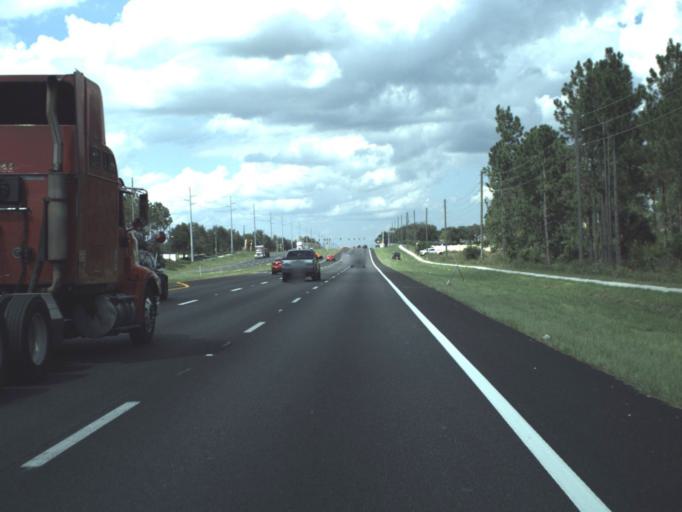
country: US
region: Florida
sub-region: Lake County
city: Four Corners
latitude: 28.3151
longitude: -81.6682
